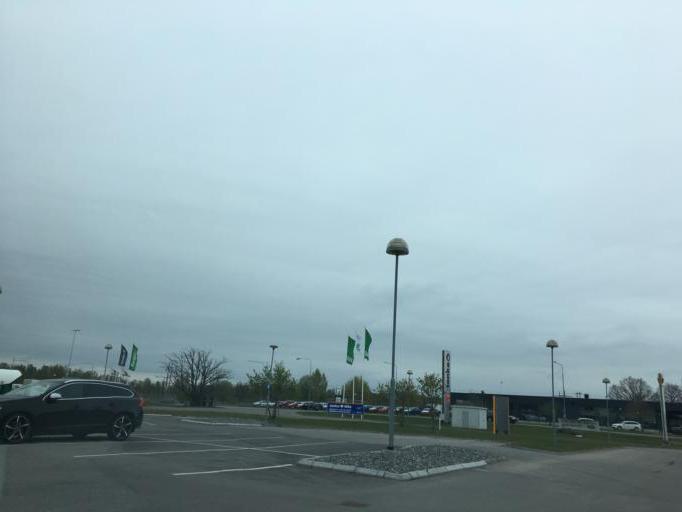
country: SE
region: Soedermanland
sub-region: Eskilstuna Kommun
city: Torshalla
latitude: 59.3884
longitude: 16.4682
